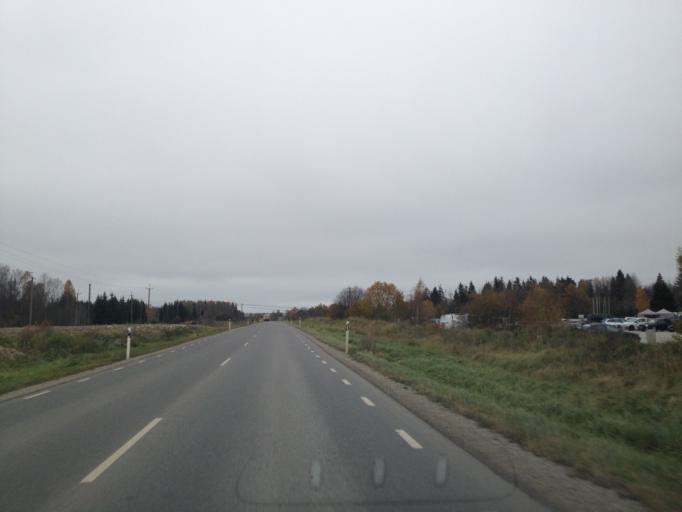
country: EE
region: Harju
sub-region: Harku vald
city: Tabasalu
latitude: 59.4108
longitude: 24.5457
